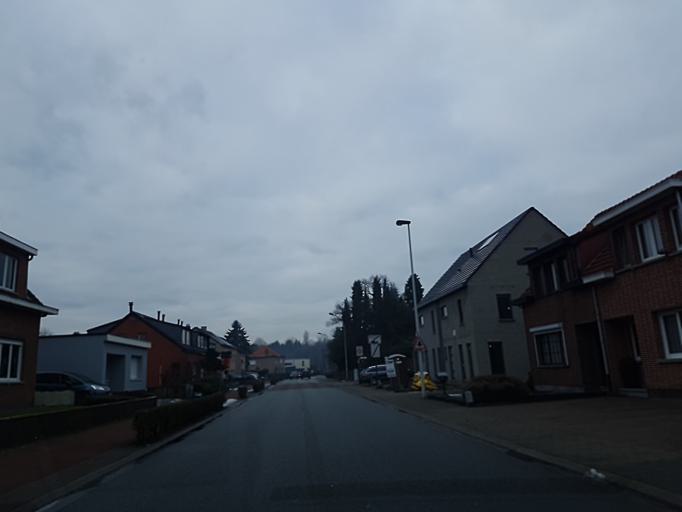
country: BE
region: Flanders
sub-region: Provincie Antwerpen
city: Lier
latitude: 51.1535
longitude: 4.6142
